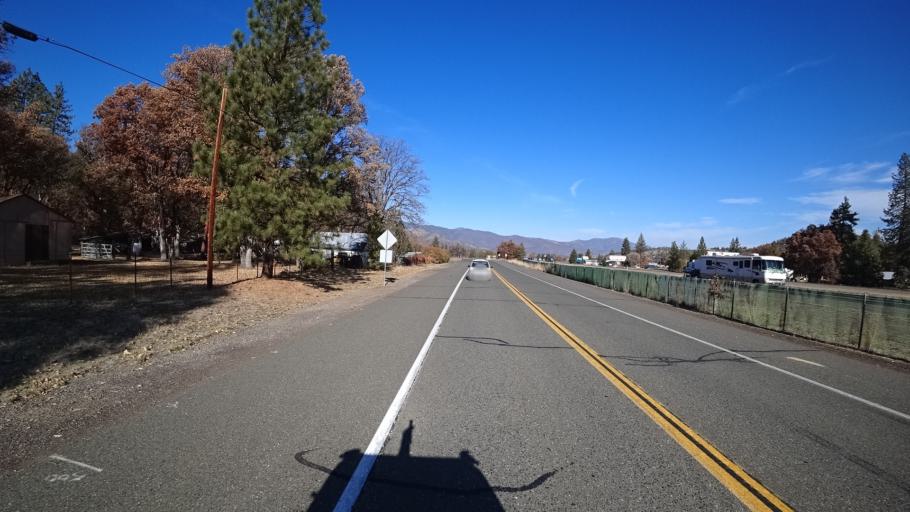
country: US
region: California
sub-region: Siskiyou County
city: Yreka
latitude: 41.6871
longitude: -122.6371
